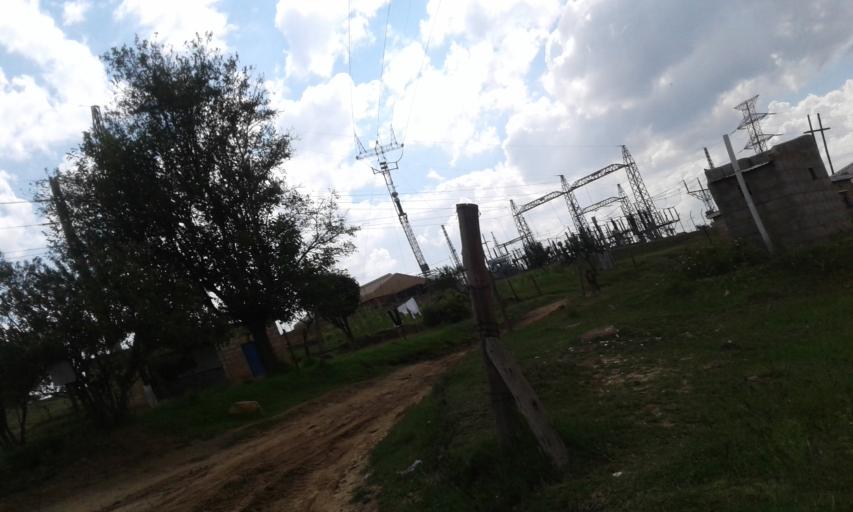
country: LS
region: Maseru
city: Maseru
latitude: -29.4068
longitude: 27.5641
